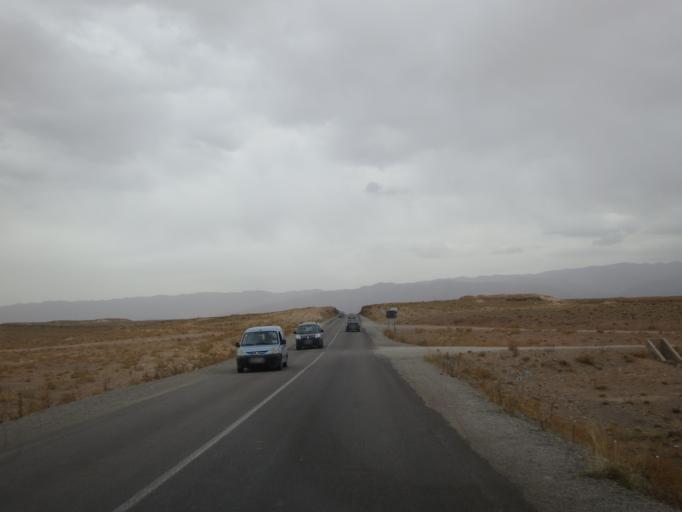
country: MA
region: Meknes-Tafilalet
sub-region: Khenifra
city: Midelt
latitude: 32.7418
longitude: -4.9121
